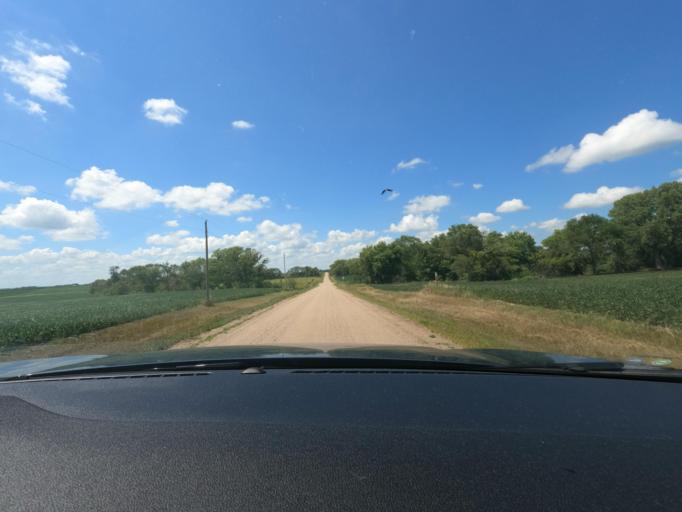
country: US
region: Nebraska
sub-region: Saunders County
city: Wahoo
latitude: 41.2491
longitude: -96.5435
